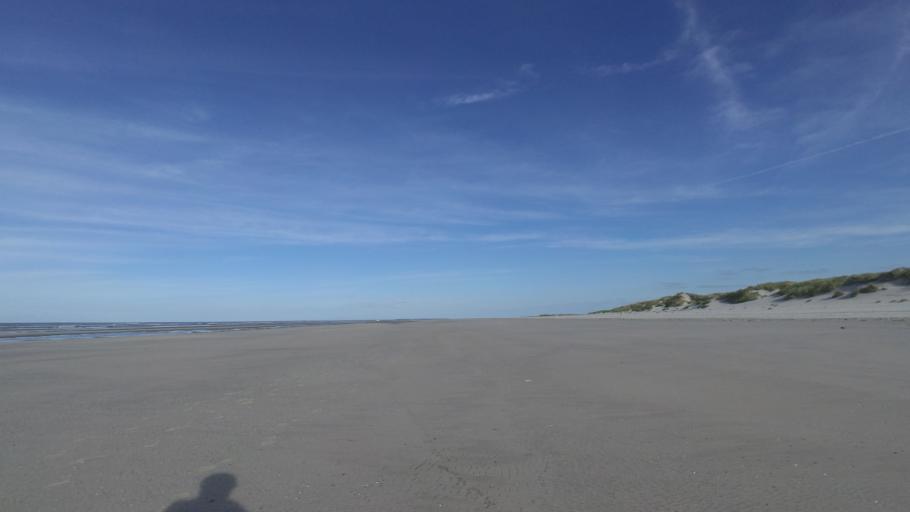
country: NL
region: Friesland
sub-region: Gemeente Dongeradeel
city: Ternaard
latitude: 53.4680
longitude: 5.9157
